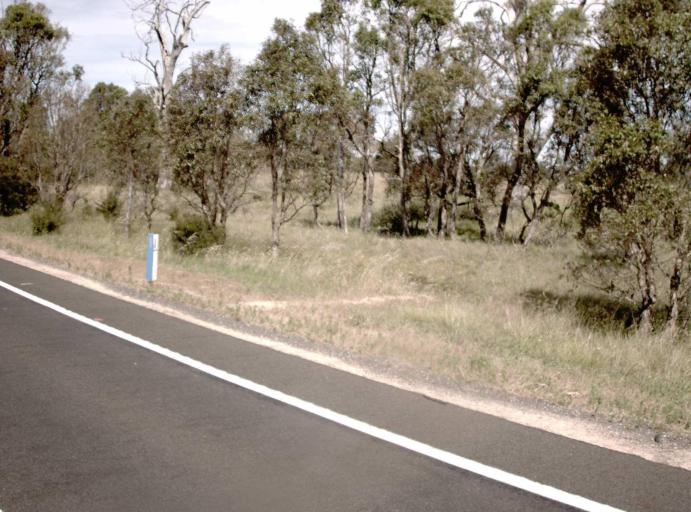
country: AU
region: Victoria
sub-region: East Gippsland
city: Bairnsdale
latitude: -37.8679
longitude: 147.4820
